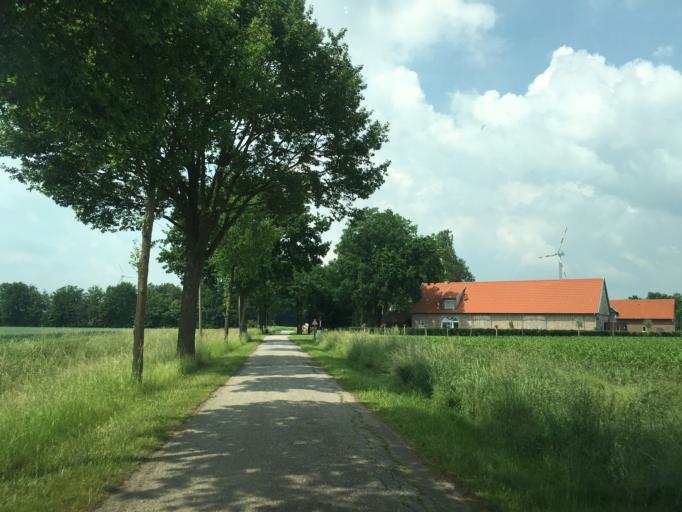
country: DE
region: North Rhine-Westphalia
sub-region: Regierungsbezirk Munster
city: Greven
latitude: 52.0340
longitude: 7.5695
